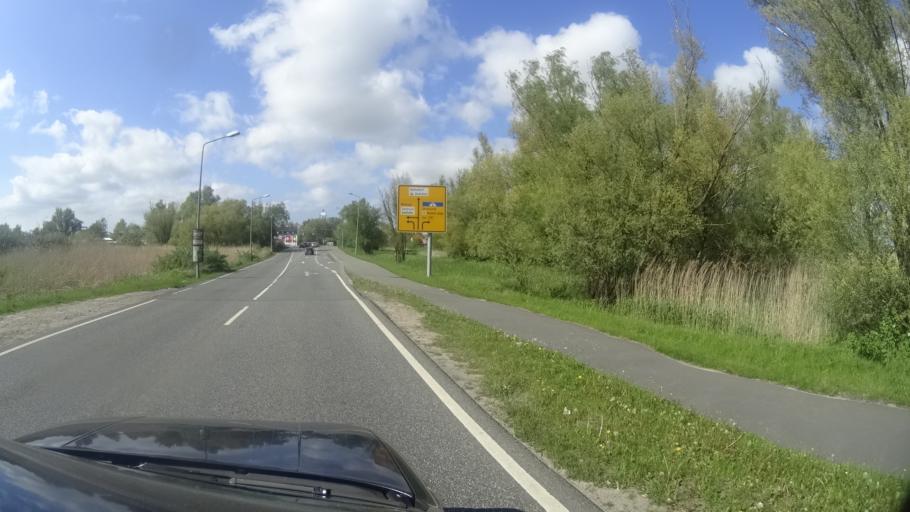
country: DE
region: Mecklenburg-Vorpommern
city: Dierkow-Neu
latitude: 54.0892
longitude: 12.1626
